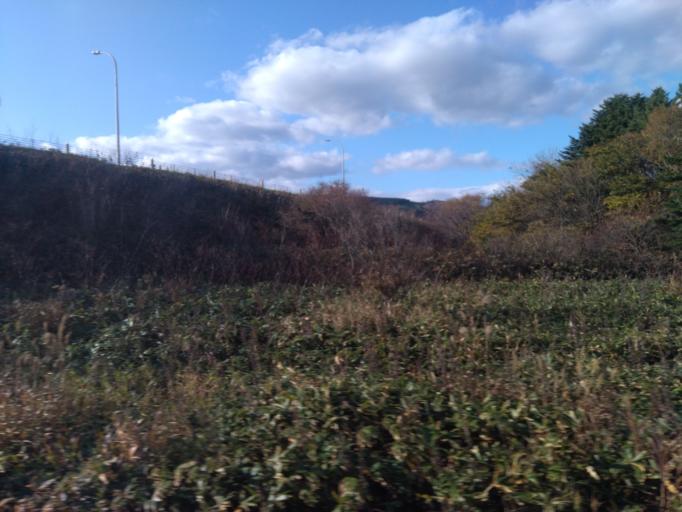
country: JP
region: Hokkaido
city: Niseko Town
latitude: 42.5802
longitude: 140.4550
